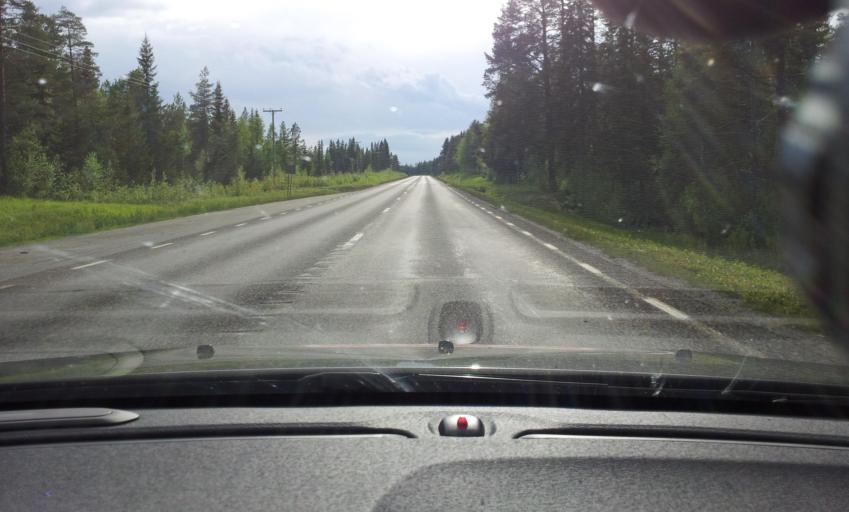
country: SE
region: Jaemtland
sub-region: OEstersunds Kommun
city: Lit
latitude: 63.2046
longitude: 14.8404
